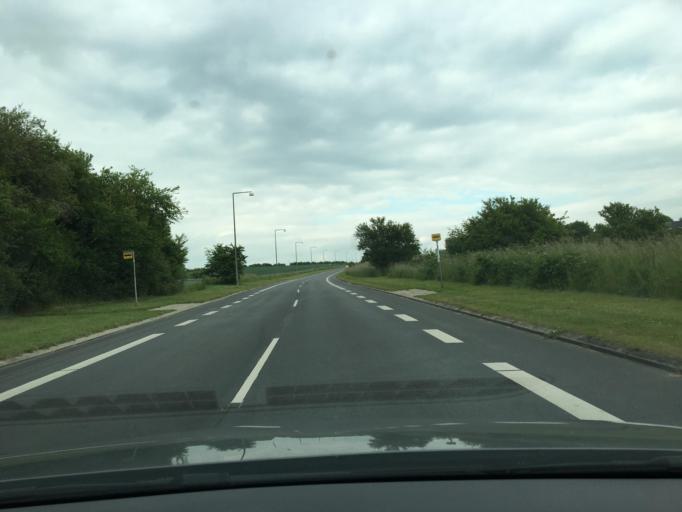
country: DK
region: South Denmark
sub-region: Assens Kommune
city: Assens
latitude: 55.2762
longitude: 9.9011
